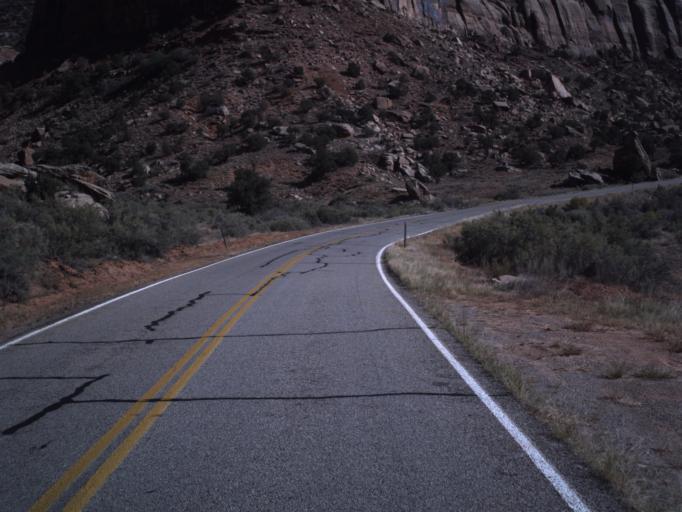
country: US
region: Utah
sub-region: San Juan County
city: Monticello
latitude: 38.0462
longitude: -109.5522
